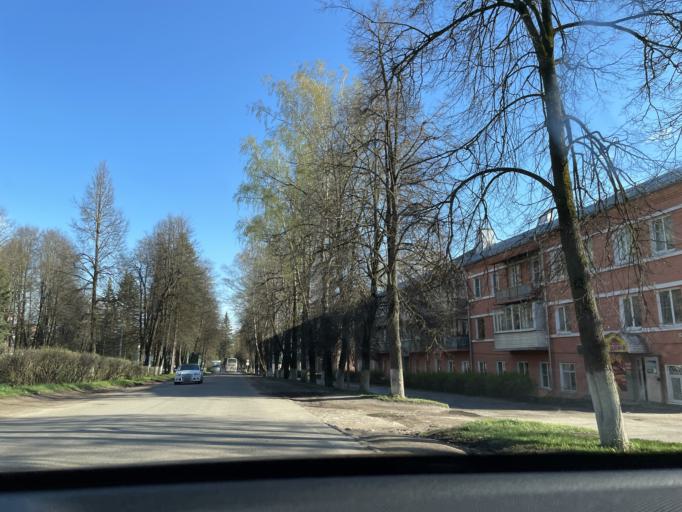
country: RU
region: Tula
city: Aleksin
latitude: 54.4849
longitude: 36.9875
